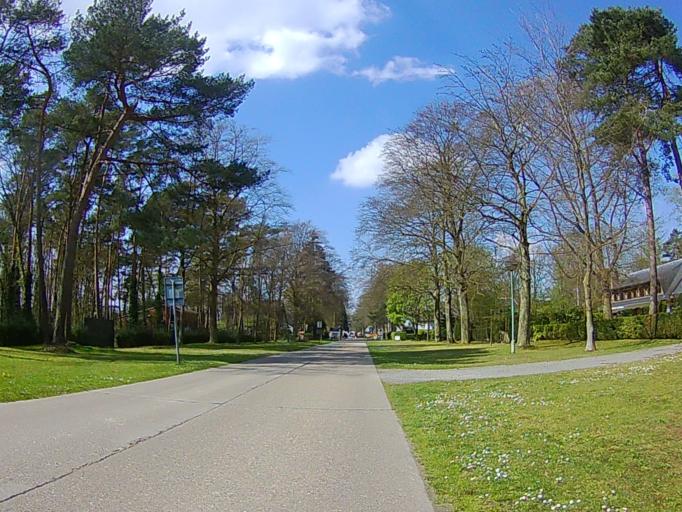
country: BE
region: Flanders
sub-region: Provincie Antwerpen
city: Wijnegem
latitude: 51.2249
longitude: 4.5510
